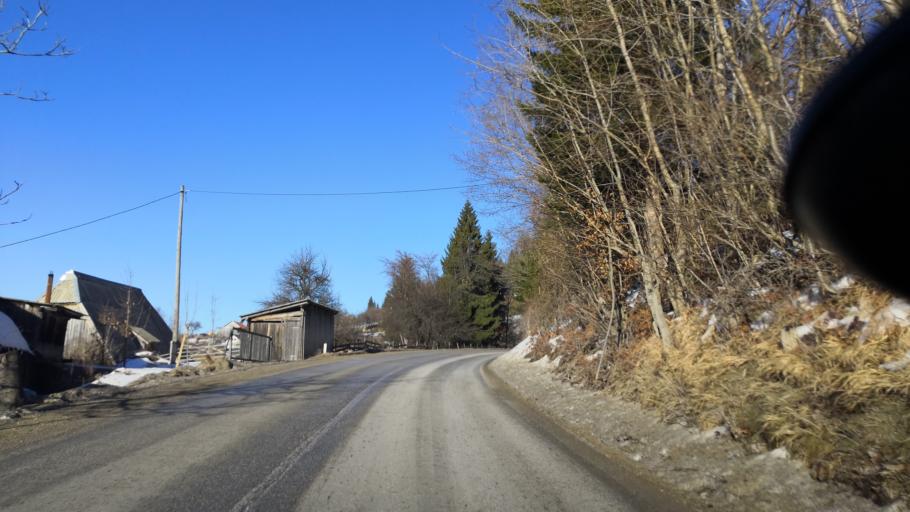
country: BA
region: Republika Srpska
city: Pale
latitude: 43.9011
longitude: 18.6365
